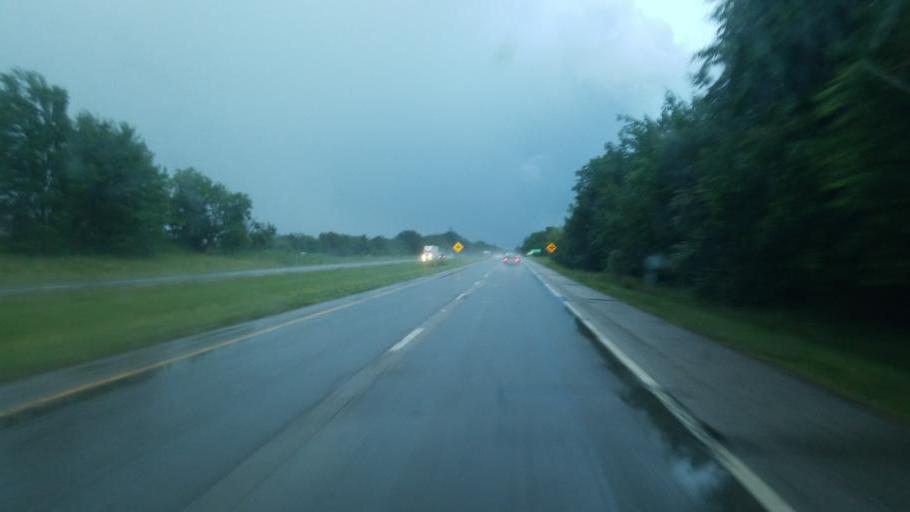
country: US
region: Ohio
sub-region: Wayne County
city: Doylestown
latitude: 40.9748
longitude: -81.6620
